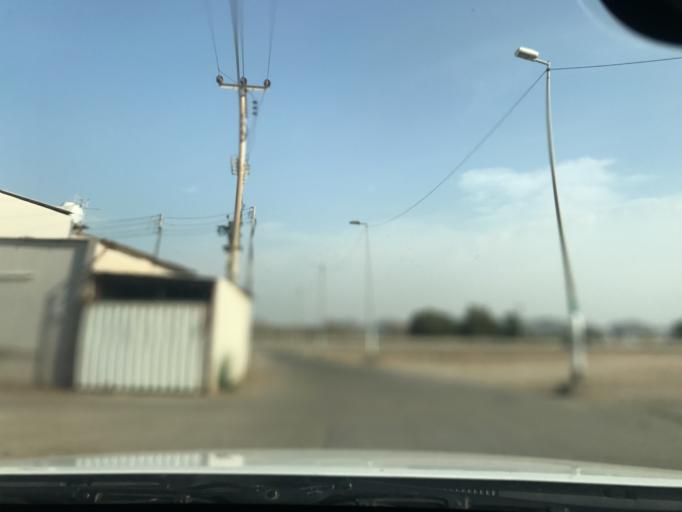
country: SA
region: Makkah
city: Al Jumum
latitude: 21.4427
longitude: 39.5353
